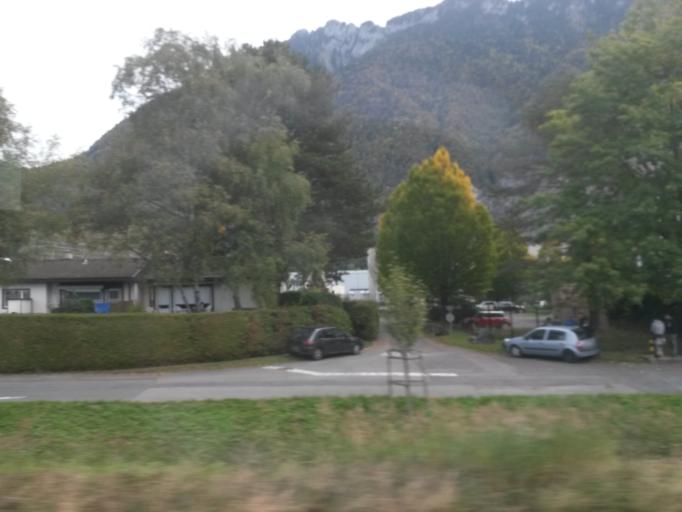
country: CH
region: Vaud
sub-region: Aigle District
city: Villeneuve
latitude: 46.3901
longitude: 6.9277
